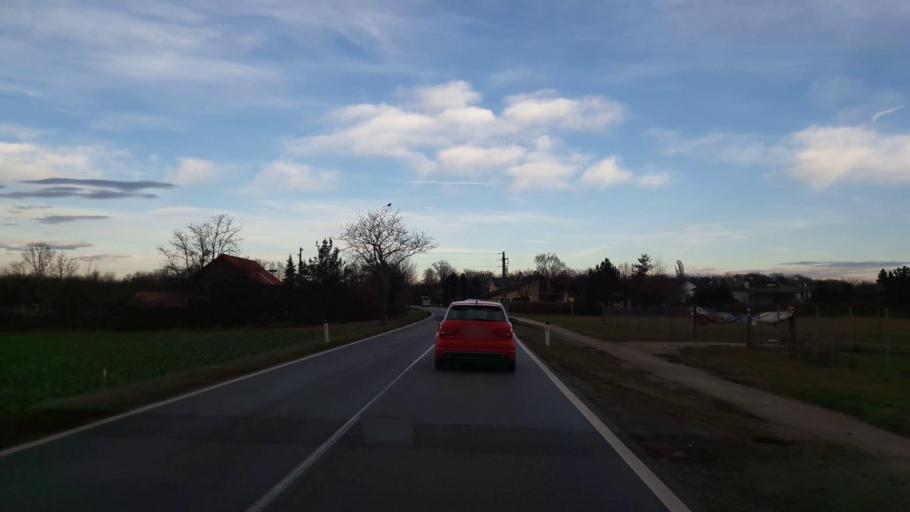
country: AT
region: Lower Austria
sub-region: Politischer Bezirk Baden
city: Ebreichsdorf
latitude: 47.9555
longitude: 16.4226
